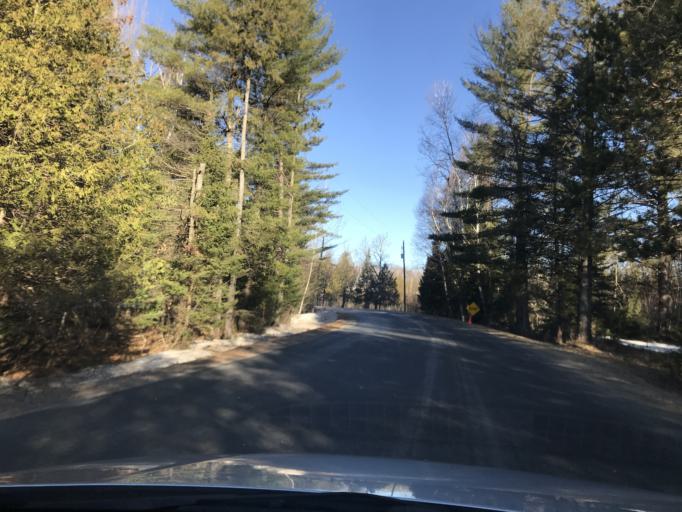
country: US
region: Wisconsin
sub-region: Marinette County
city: Niagara
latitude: 45.3787
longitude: -88.0254
